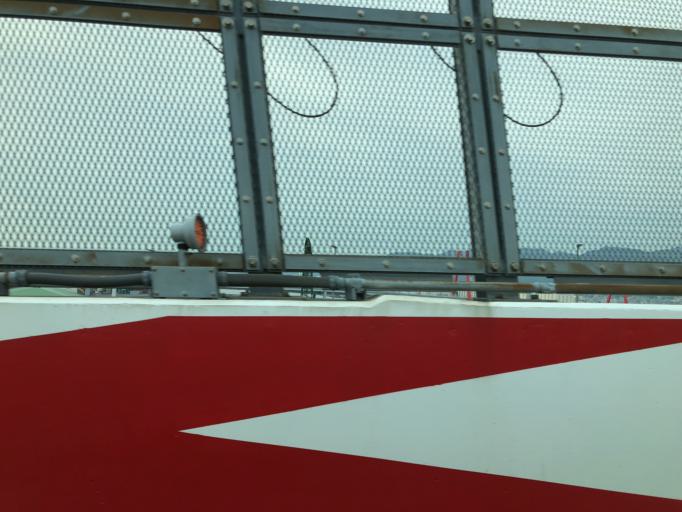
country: JP
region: Hyogo
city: Ashiya
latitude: 34.6964
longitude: 135.2731
